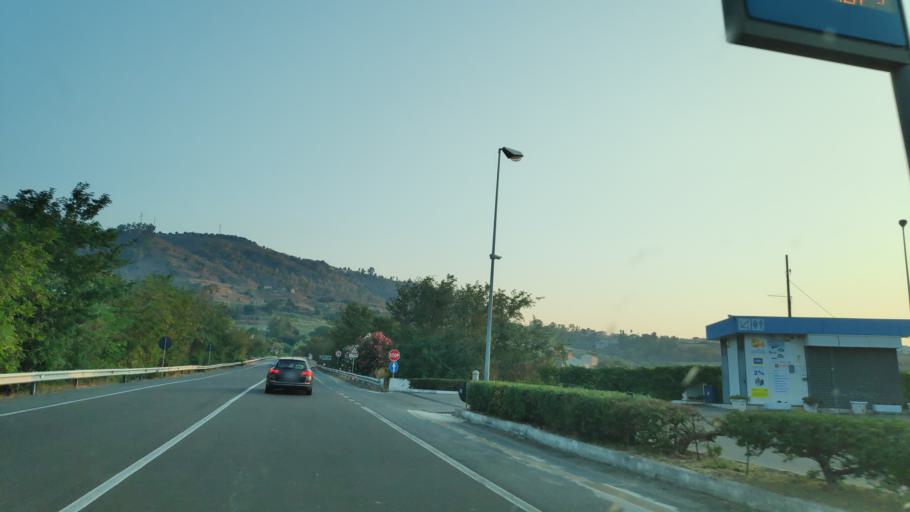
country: IT
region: Calabria
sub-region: Provincia di Catanzaro
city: Montepaone Lido
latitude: 38.7396
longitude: 16.5466
